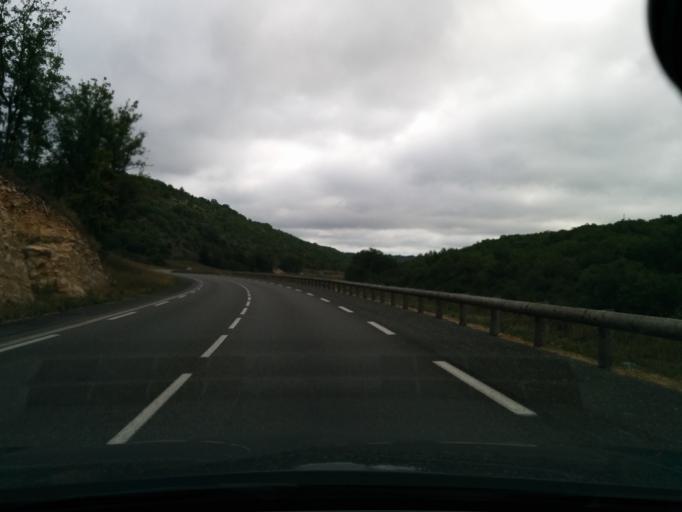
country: FR
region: Midi-Pyrenees
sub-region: Departement du Lot
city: Cahors
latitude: 44.4081
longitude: 1.4072
